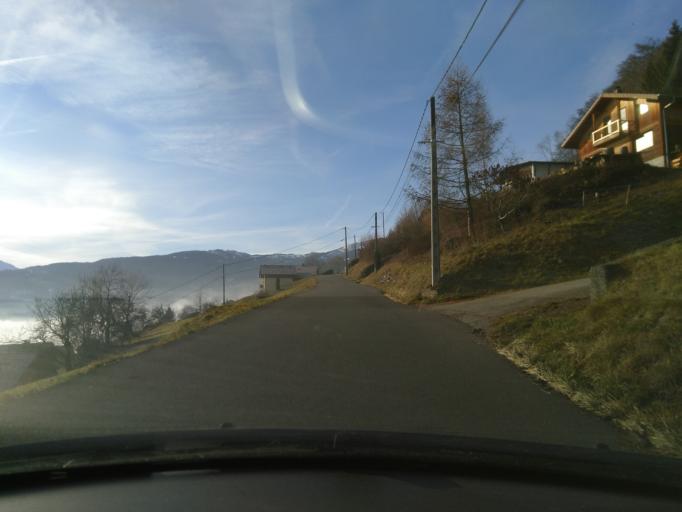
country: FR
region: Rhone-Alpes
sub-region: Departement de la Haute-Savoie
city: Sallanches
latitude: 45.9483
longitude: 6.6201
